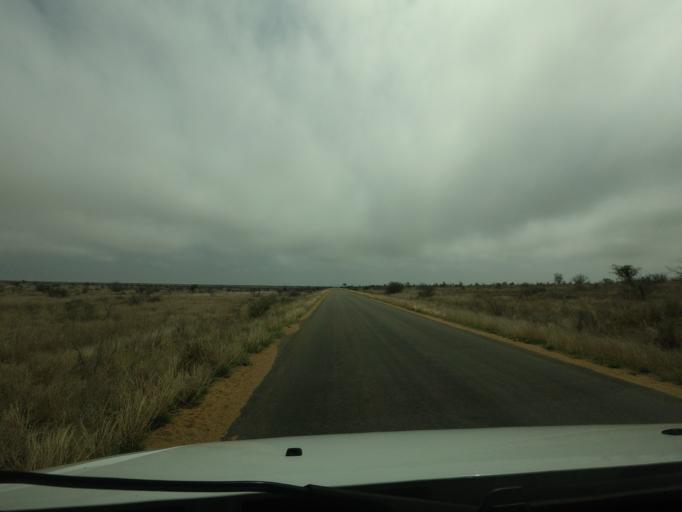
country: ZA
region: Limpopo
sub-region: Mopani District Municipality
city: Phalaborwa
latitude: -24.2068
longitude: 31.7195
